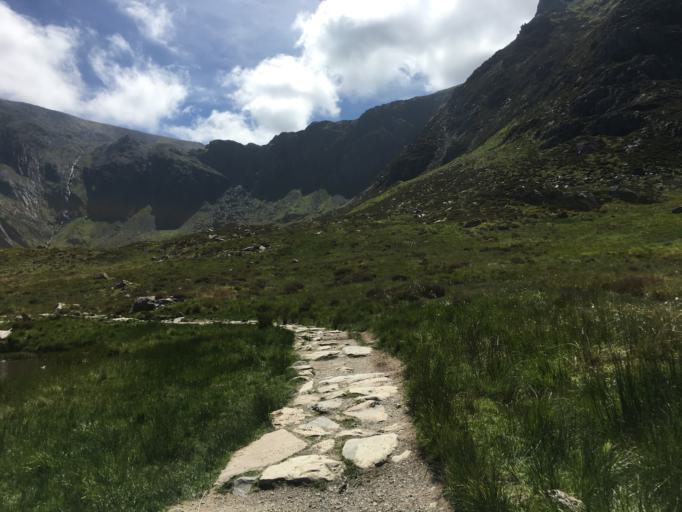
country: GB
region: Wales
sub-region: Gwynedd
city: Bethesda
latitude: 53.1183
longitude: -4.0282
